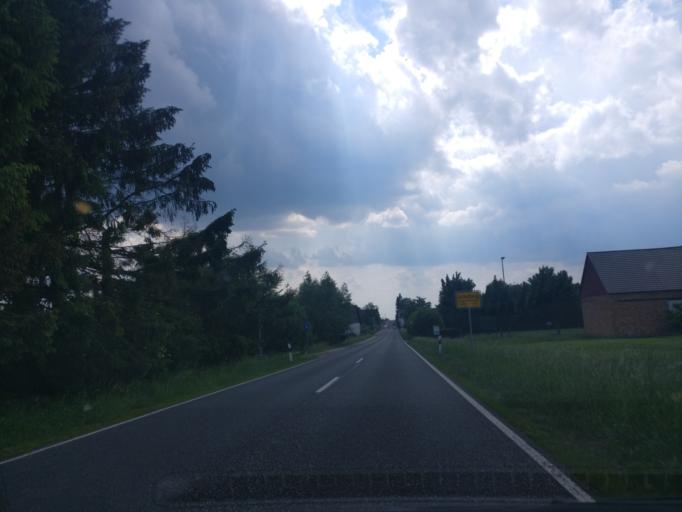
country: DE
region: Lower Saxony
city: Hannoversch Munden
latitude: 51.3755
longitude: 9.6182
